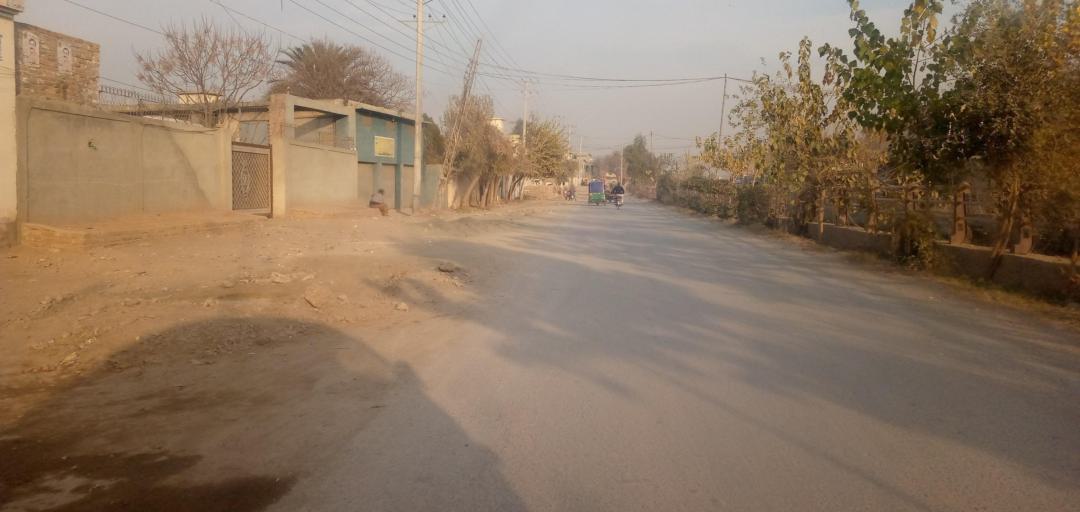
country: PK
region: Khyber Pakhtunkhwa
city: Peshawar
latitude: 33.9734
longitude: 71.5250
